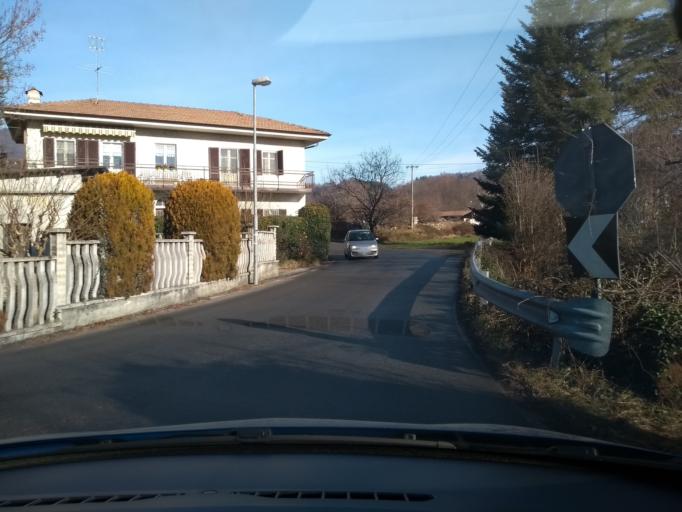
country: IT
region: Piedmont
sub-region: Provincia di Torino
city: Cuorgne
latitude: 45.4016
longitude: 7.6581
